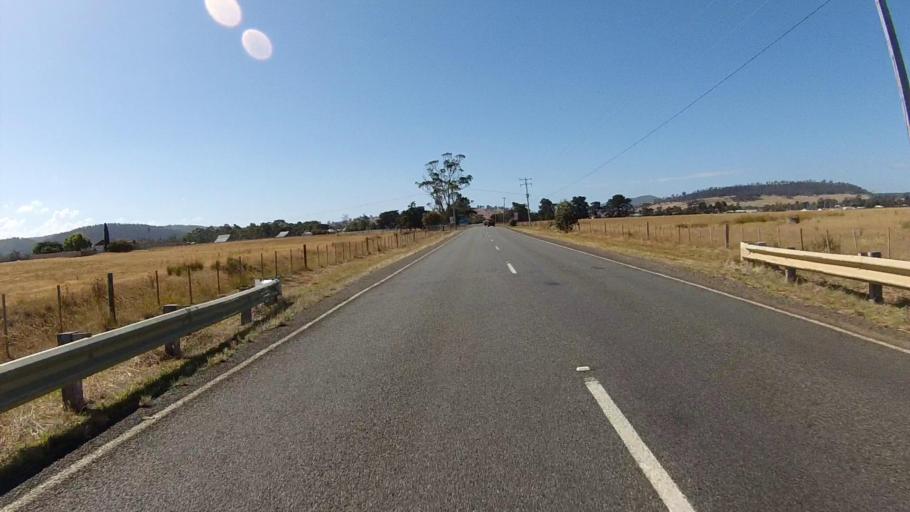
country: AU
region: Tasmania
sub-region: Sorell
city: Sorell
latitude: -42.5143
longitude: 147.9045
